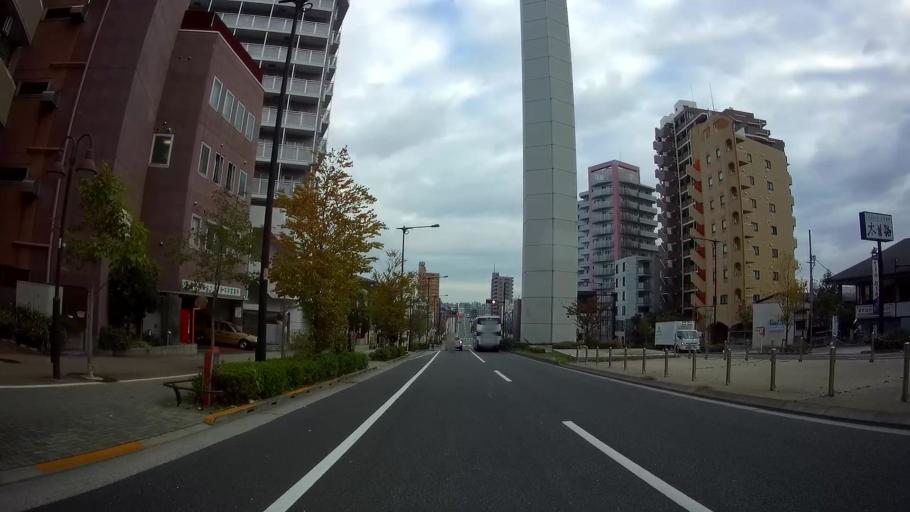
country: JP
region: Tokyo
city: Tokyo
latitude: 35.7119
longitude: 139.6856
